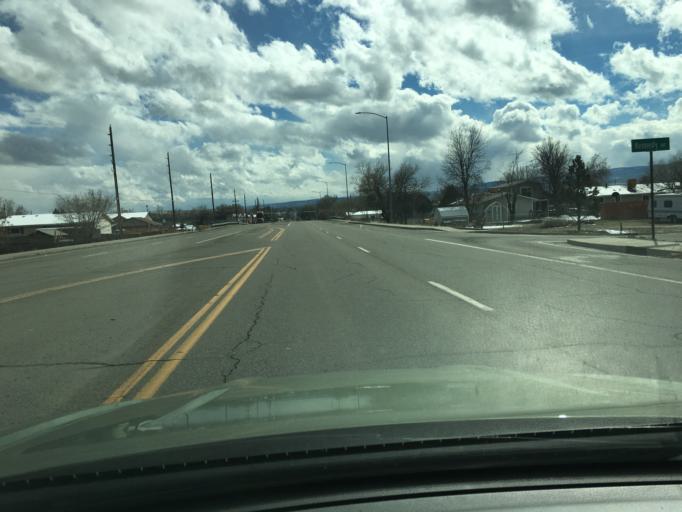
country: US
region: Colorado
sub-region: Mesa County
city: Clifton
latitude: 39.0808
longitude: -108.4595
